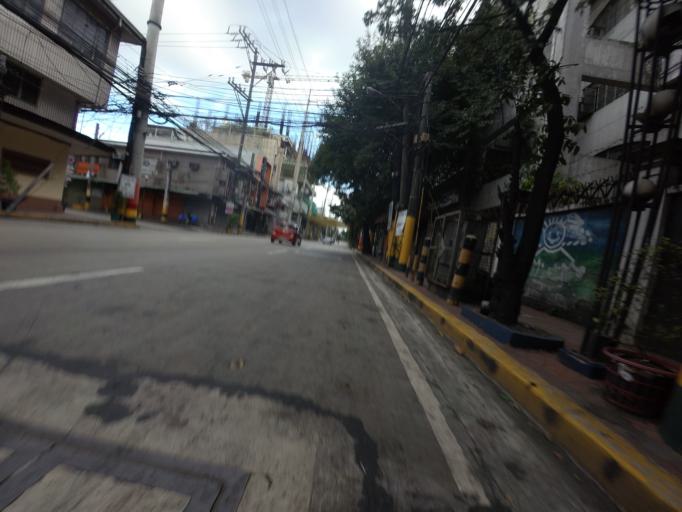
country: PH
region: Metro Manila
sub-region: City of Manila
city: Quiapo
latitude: 14.5882
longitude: 120.9849
